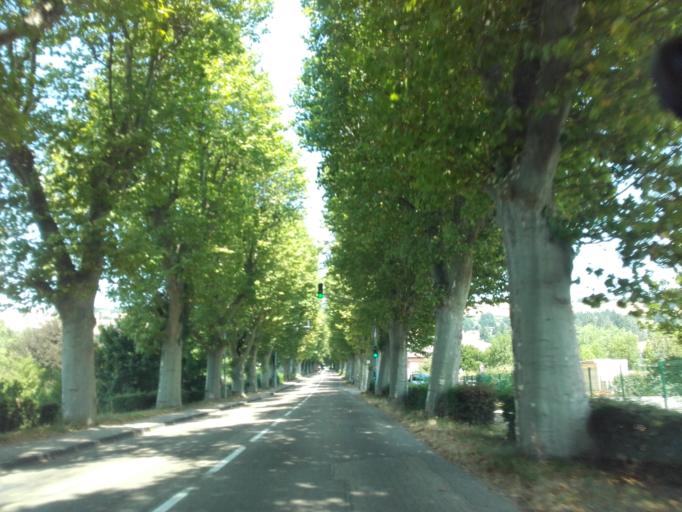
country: FR
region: Rhone-Alpes
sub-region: Departement de l'Isere
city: La Cote-Saint-Andre
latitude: 45.3879
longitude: 5.2623
